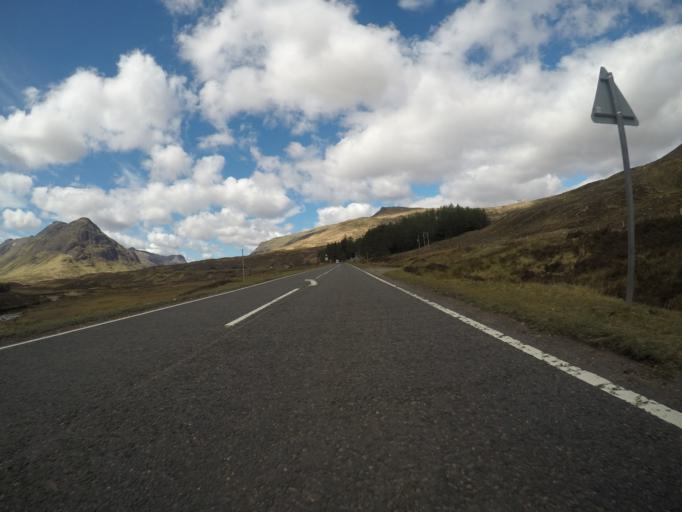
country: GB
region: Scotland
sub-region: Highland
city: Spean Bridge
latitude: 56.6637
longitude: -4.8994
